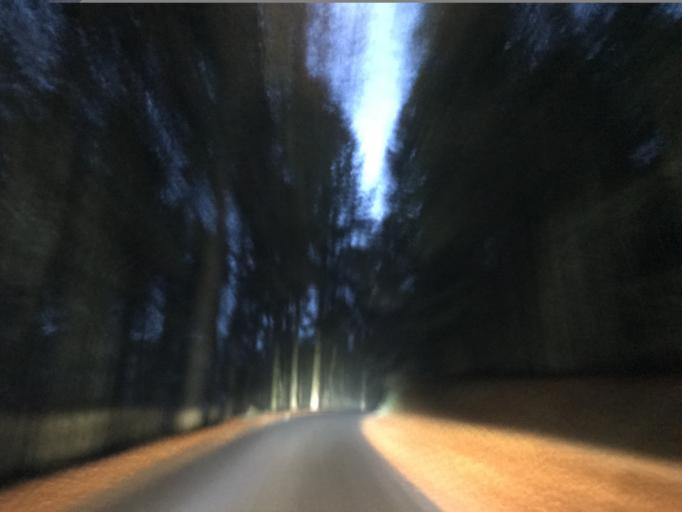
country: FR
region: Rhone-Alpes
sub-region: Departement de la Loire
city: Noiretable
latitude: 45.7668
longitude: 3.6843
